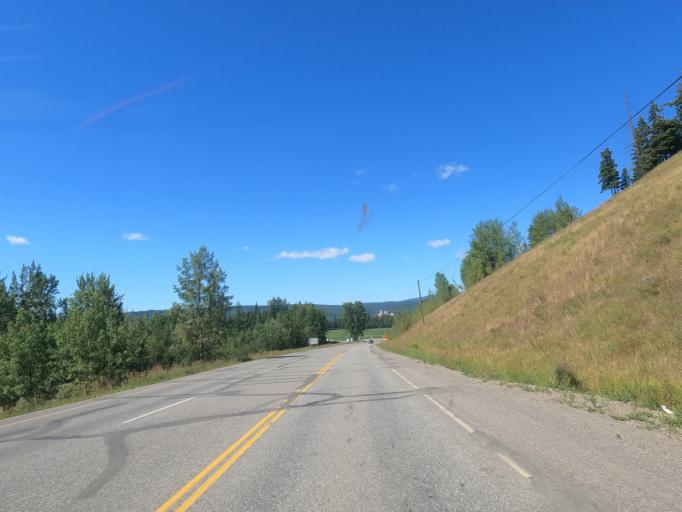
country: CA
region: British Columbia
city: Quesnel
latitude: 53.0160
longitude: -122.4897
